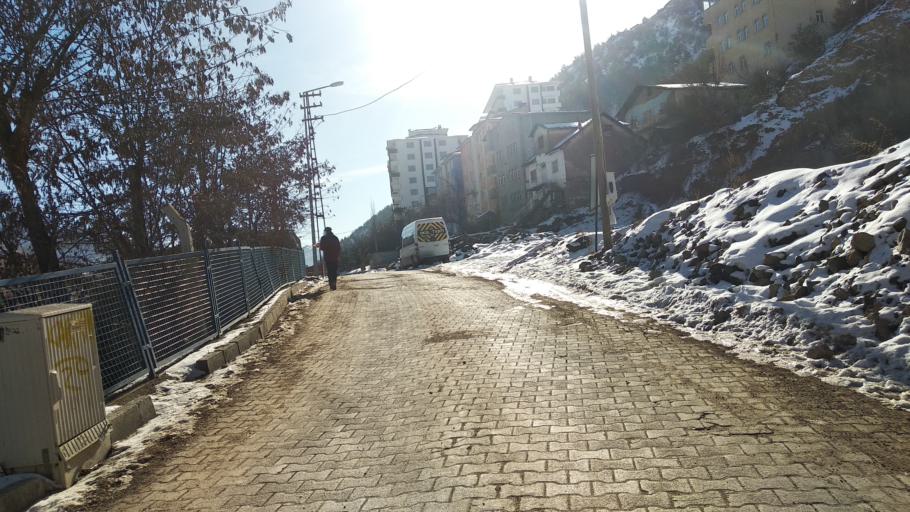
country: TR
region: Gumushane
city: Gumushkhane
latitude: 40.4559
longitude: 39.4872
